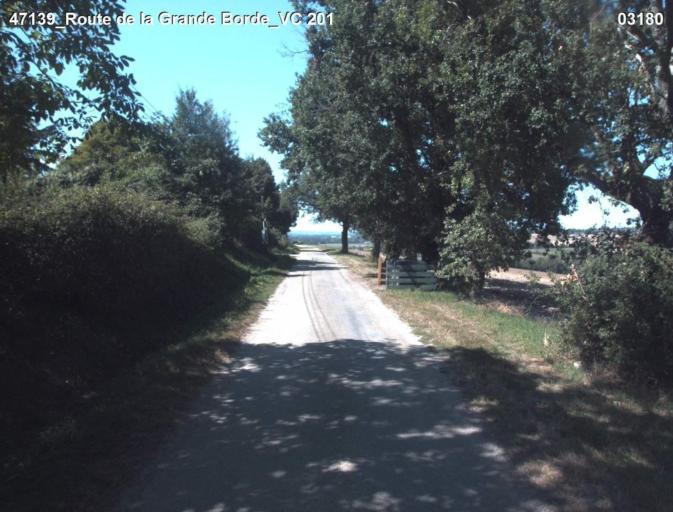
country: FR
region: Aquitaine
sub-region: Departement du Lot-et-Garonne
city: Nerac
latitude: 44.0875
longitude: 0.3813
